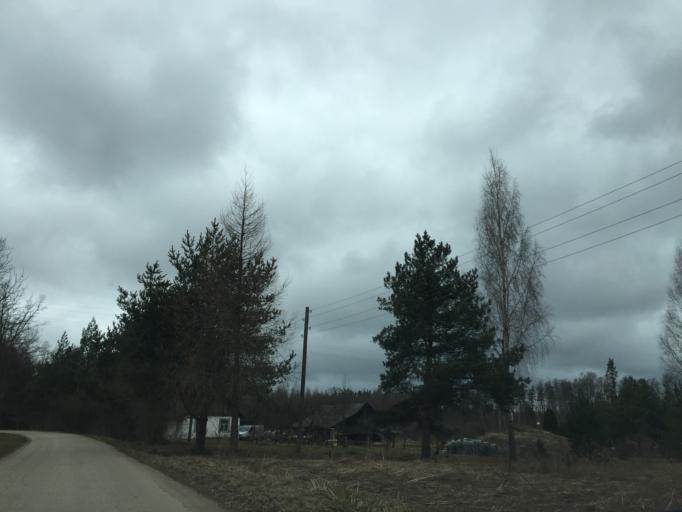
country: LV
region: Ilukste
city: Ilukste
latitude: 55.9071
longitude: 26.3681
